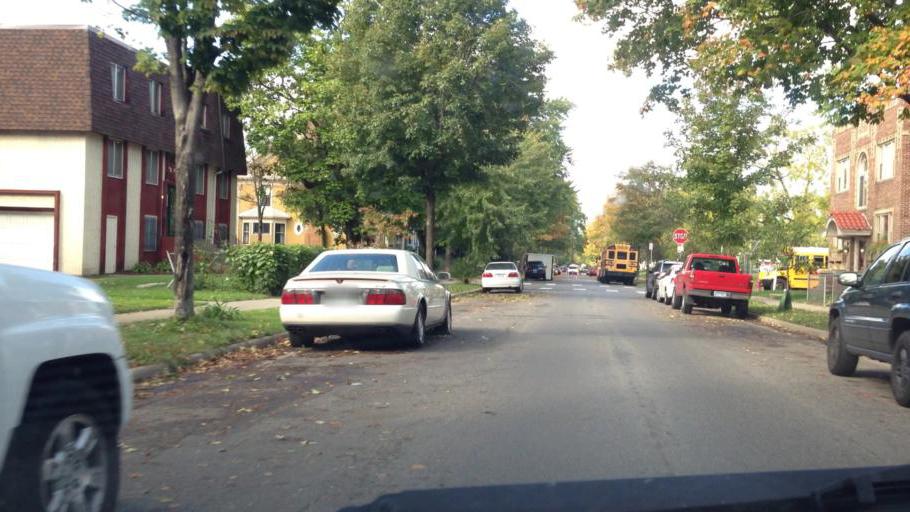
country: US
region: Minnesota
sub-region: Hennepin County
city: Minneapolis
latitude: 44.9532
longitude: -93.2855
